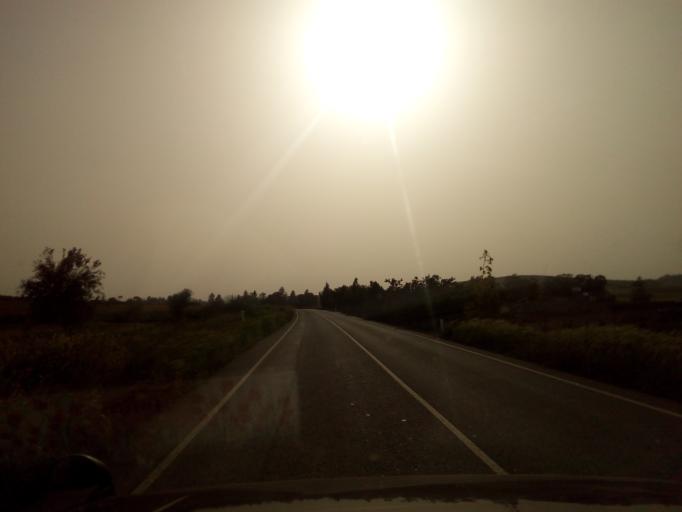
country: CY
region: Larnaka
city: Athienou
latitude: 35.0503
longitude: 33.5027
